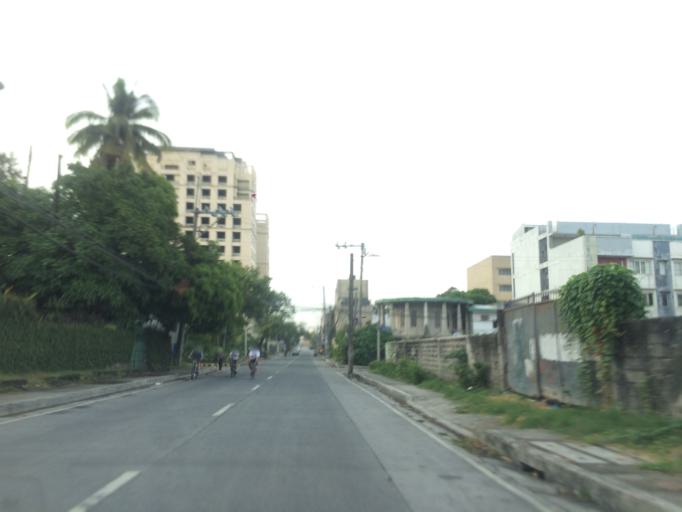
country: PH
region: Calabarzon
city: Del Monte
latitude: 14.6330
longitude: 121.0044
